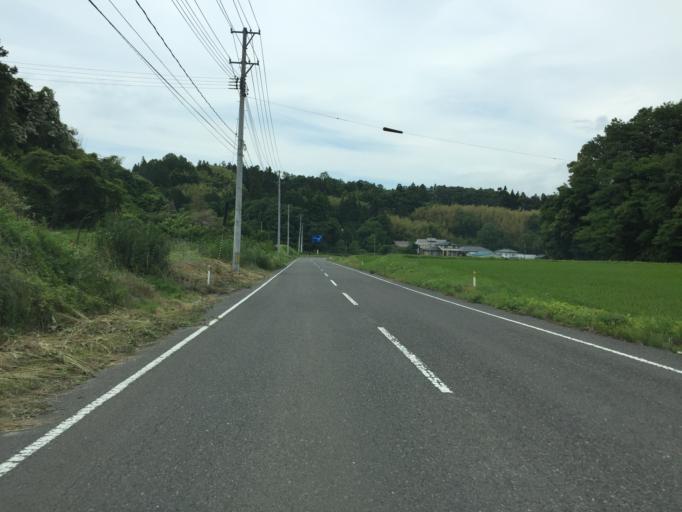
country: JP
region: Fukushima
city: Funehikimachi-funehiki
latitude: 37.4149
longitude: 140.6495
